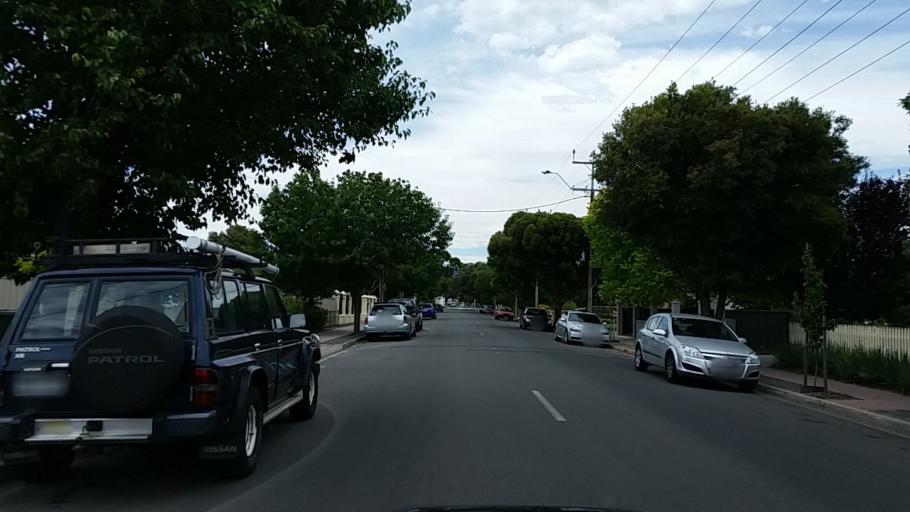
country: AU
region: South Australia
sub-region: Norwood Payneham St Peters
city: Trinity Gardens
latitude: -34.9061
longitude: 138.6434
